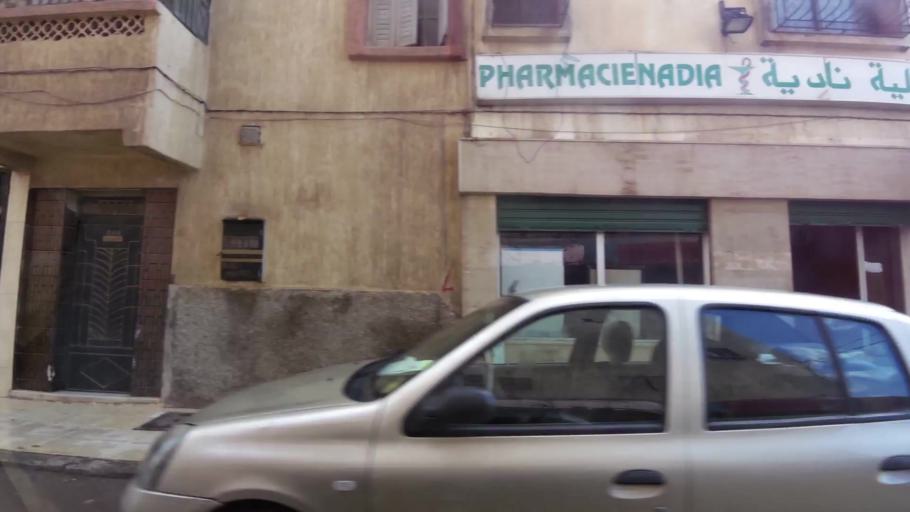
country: MA
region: Grand Casablanca
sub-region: Casablanca
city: Casablanca
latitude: 33.5305
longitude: -7.6698
